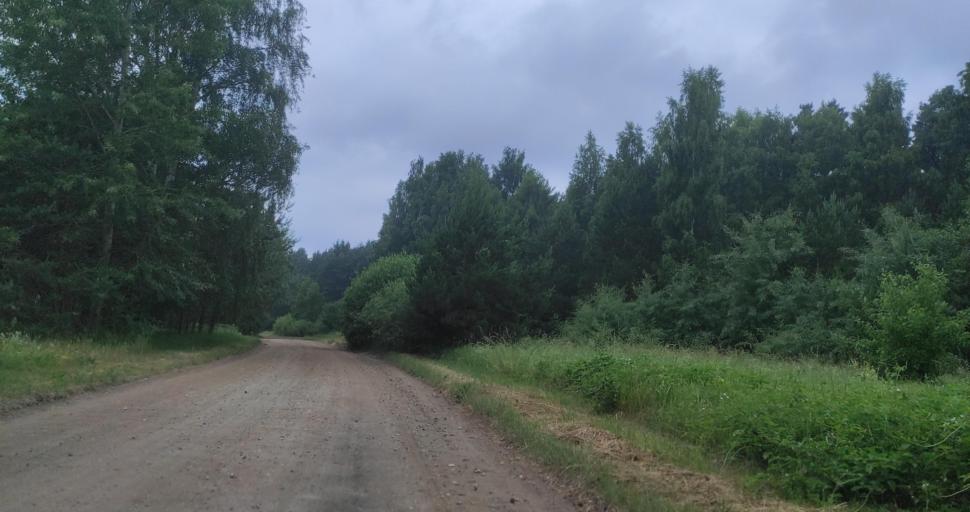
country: LV
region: Pavilostas
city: Pavilosta
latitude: 56.8852
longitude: 21.2071
